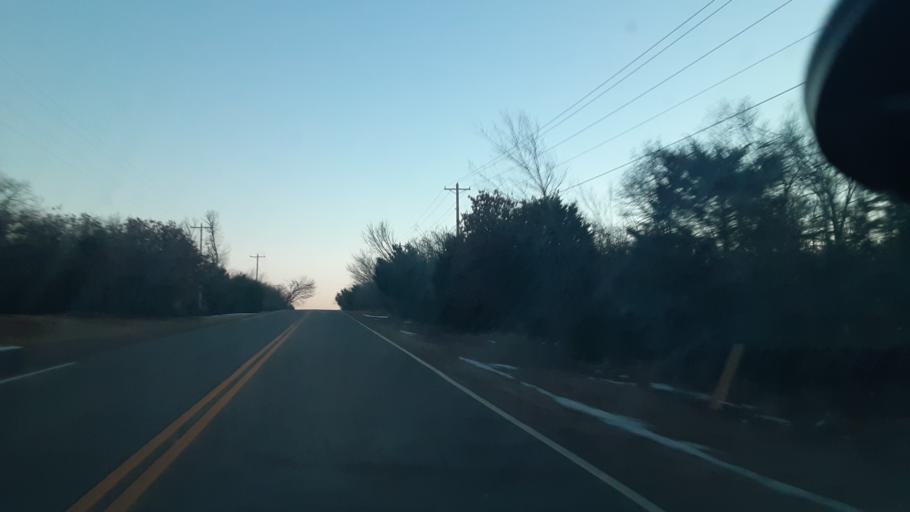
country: US
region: Oklahoma
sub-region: Oklahoma County
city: Edmond
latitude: 35.7079
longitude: -97.4252
